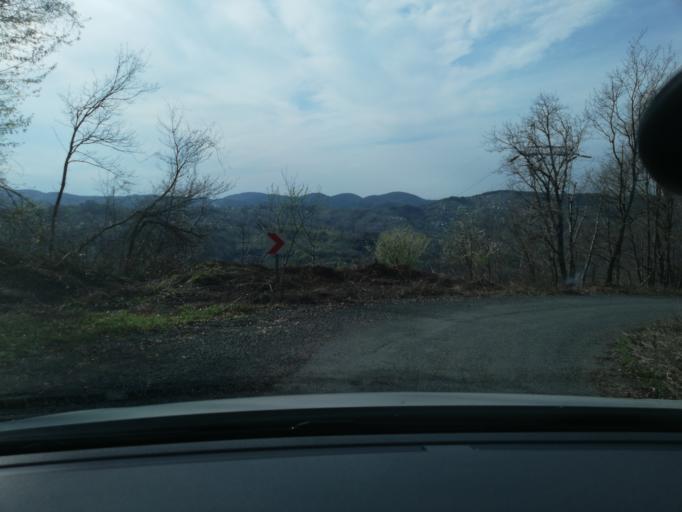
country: TR
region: Zonguldak
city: Kozlu
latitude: 41.3534
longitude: 31.6298
